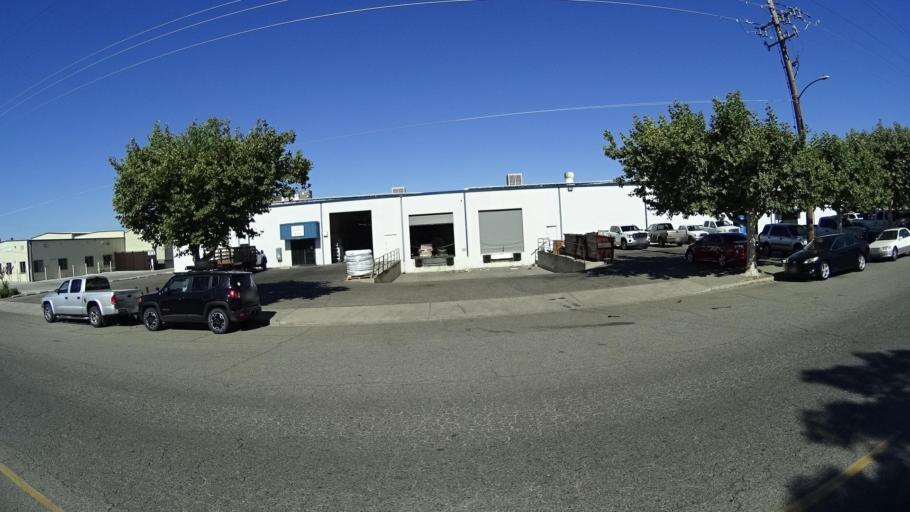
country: US
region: California
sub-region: Fresno County
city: Fresno
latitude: 36.7017
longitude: -119.7817
